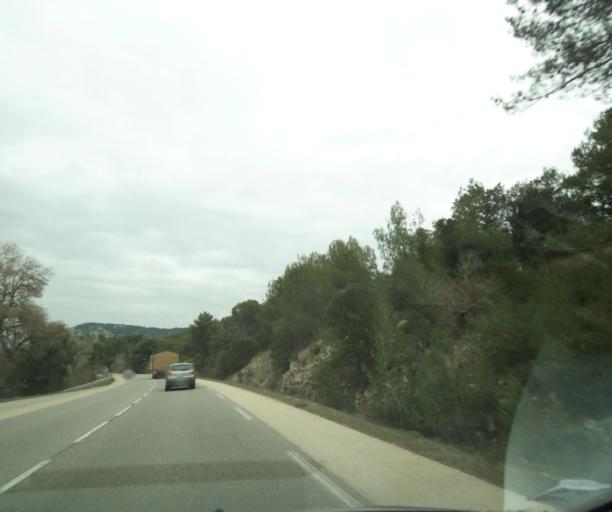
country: FR
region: Provence-Alpes-Cote d'Azur
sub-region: Departement des Bouches-du-Rhone
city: Jouques
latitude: 43.6671
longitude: 5.6466
